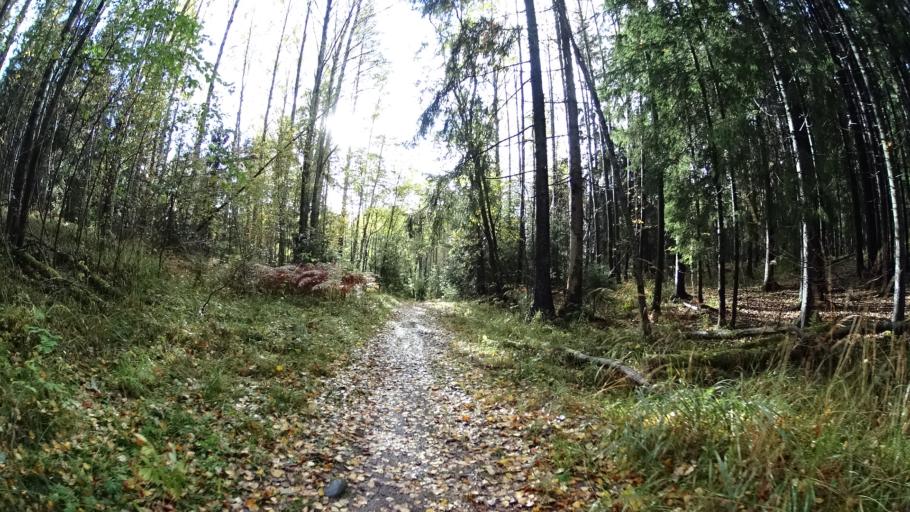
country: FI
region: Uusimaa
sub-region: Helsinki
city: Kilo
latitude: 60.2940
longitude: 24.8017
